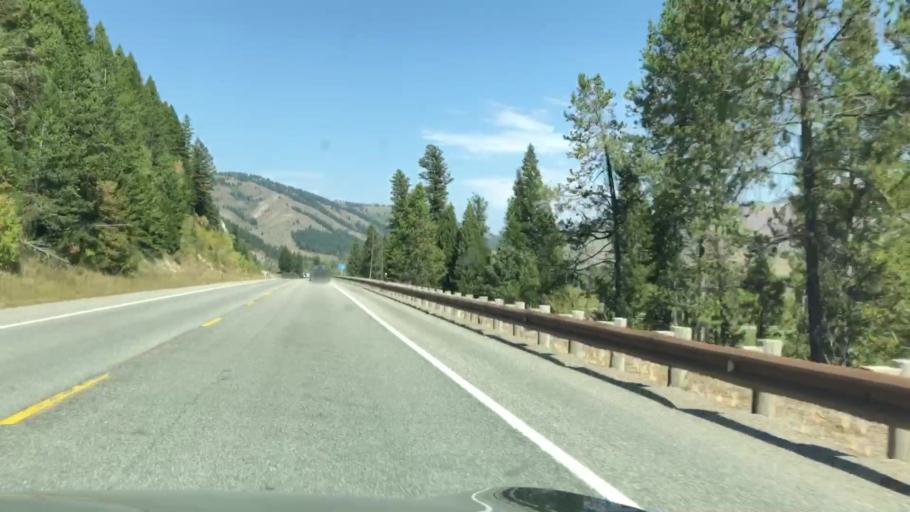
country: US
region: Wyoming
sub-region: Teton County
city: Hoback
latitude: 43.2657
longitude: -110.7853
